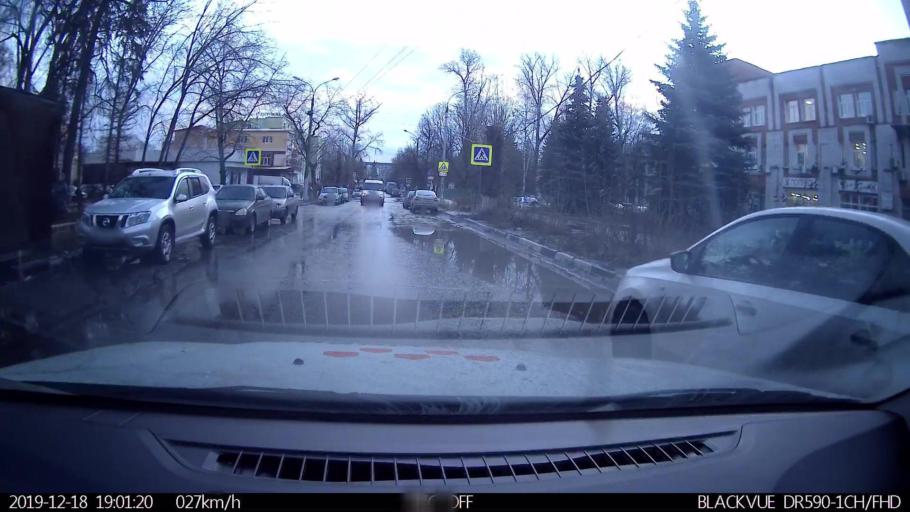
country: RU
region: Nizjnij Novgorod
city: Gorbatovka
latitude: 56.3287
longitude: 43.8539
